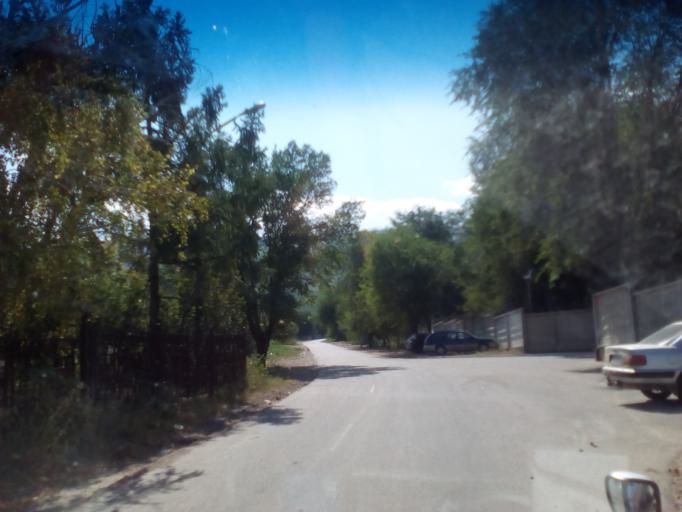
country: KZ
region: Almaty Oblysy
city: Burunday
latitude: 43.1600
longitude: 76.3825
